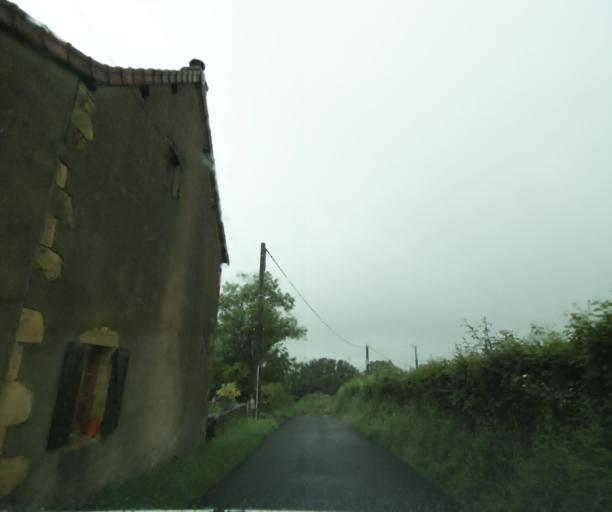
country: FR
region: Bourgogne
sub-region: Departement de Saone-et-Loire
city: Charolles
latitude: 46.3526
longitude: 4.2199
